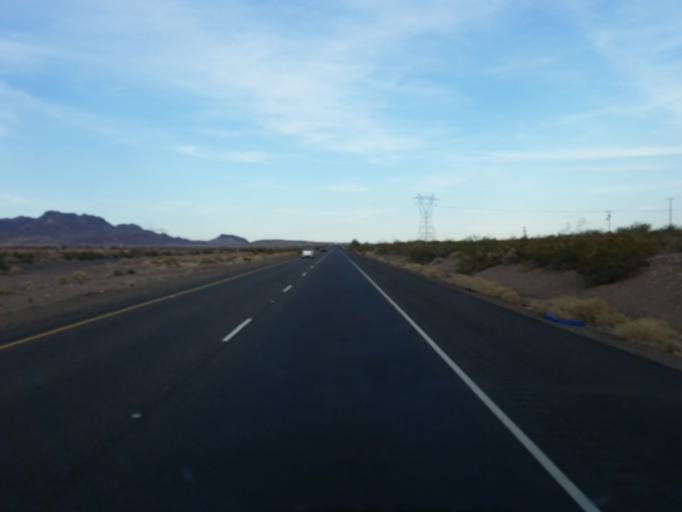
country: US
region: California
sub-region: San Bernardino County
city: Fort Irwin
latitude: 34.7753
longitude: -116.3806
